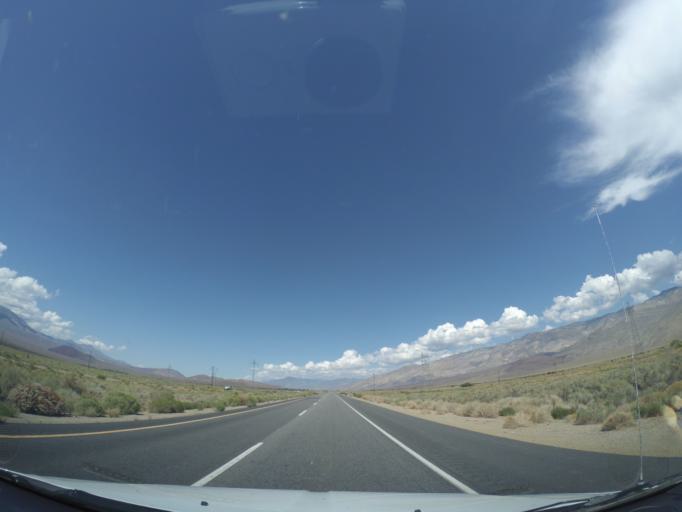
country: US
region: California
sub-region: Inyo County
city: Big Pine
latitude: 36.9730
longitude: -118.2372
